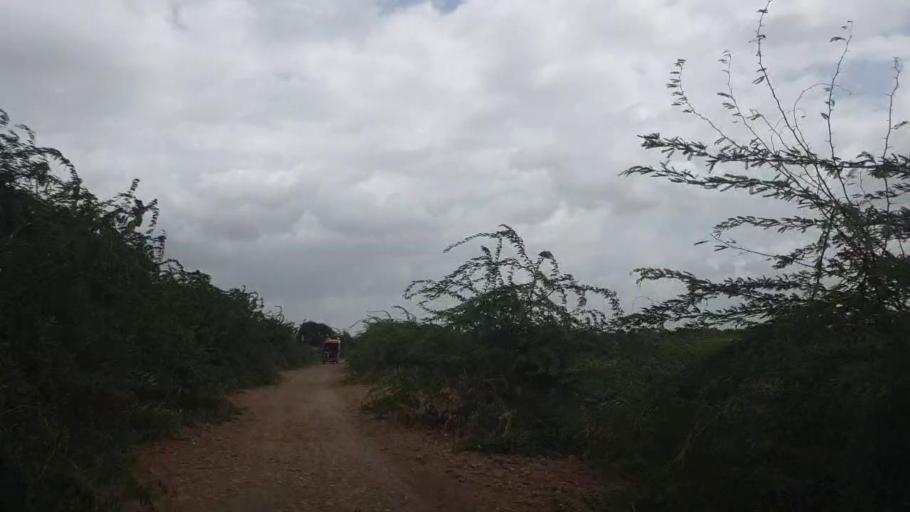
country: PK
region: Sindh
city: Badin
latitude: 24.6422
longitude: 68.9472
